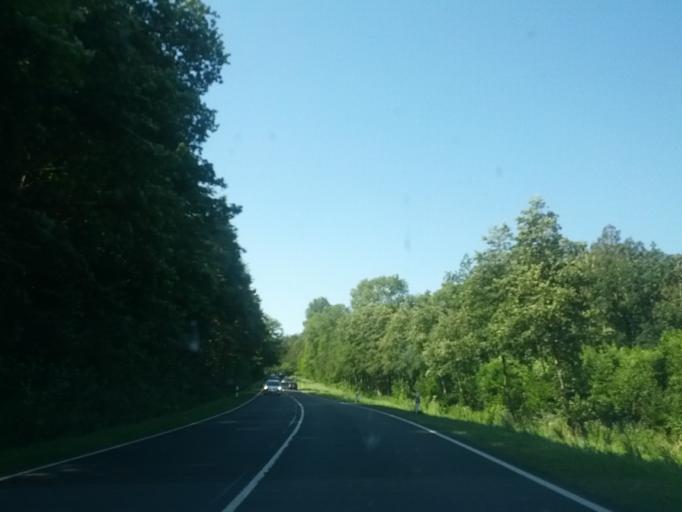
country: DE
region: Mecklenburg-Vorpommern
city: Sagard
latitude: 54.4807
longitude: 13.4872
